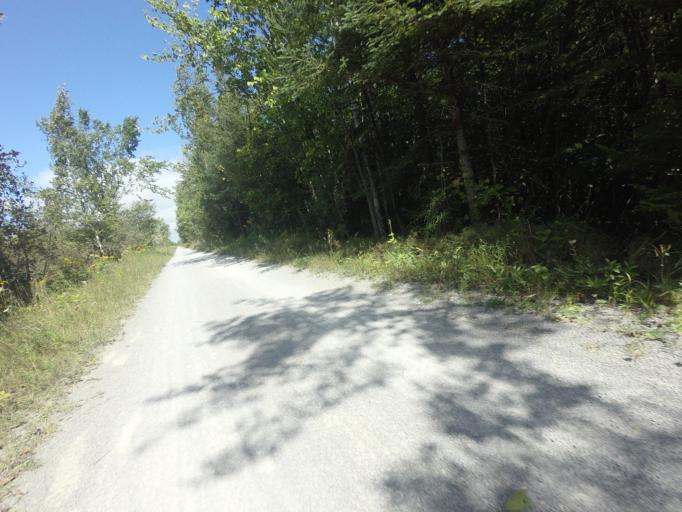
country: CA
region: Ontario
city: Uxbridge
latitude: 44.1332
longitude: -79.0947
